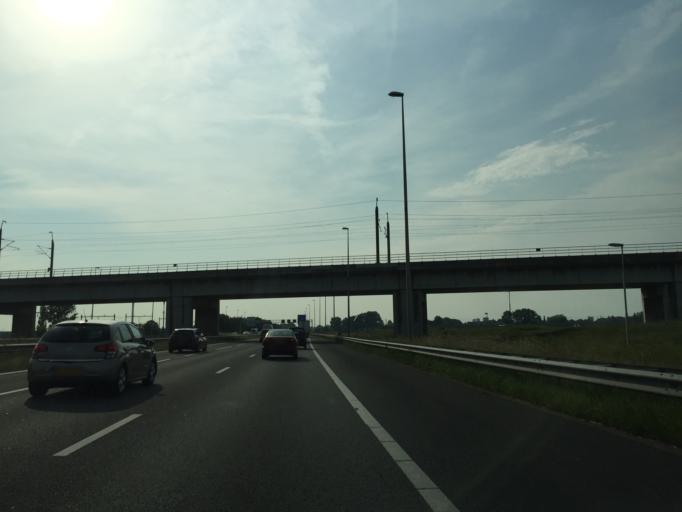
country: NL
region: South Holland
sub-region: Gemeente Lansingerland
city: Bleiswijk
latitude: 52.0388
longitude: 4.5302
